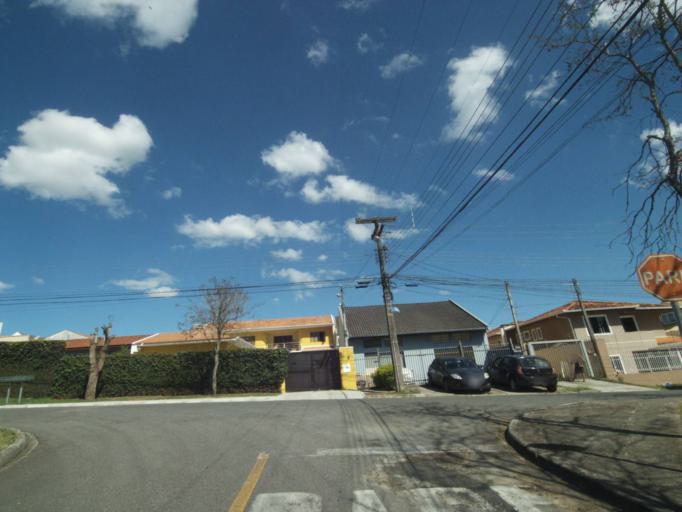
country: BR
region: Parana
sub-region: Curitiba
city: Curitiba
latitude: -25.3754
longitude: -49.2478
